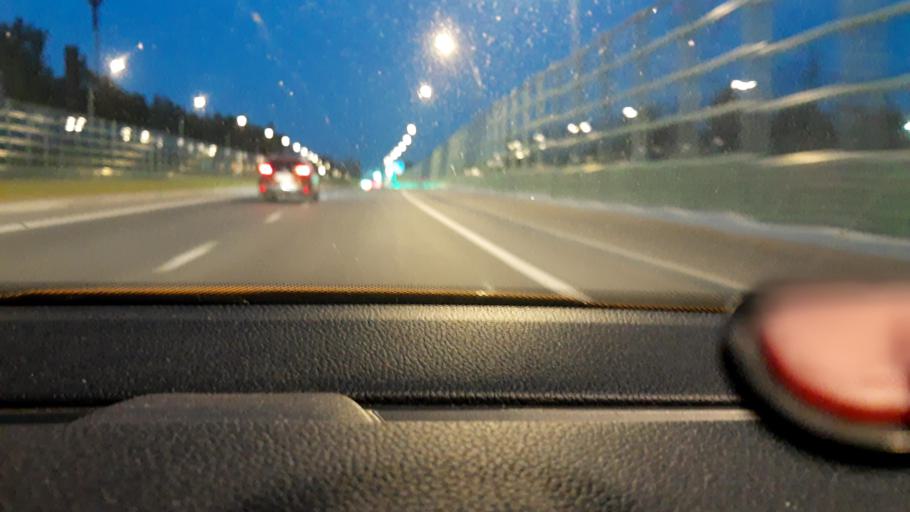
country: RU
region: Moskovskaya
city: Filimonki
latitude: 55.5687
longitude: 37.3528
